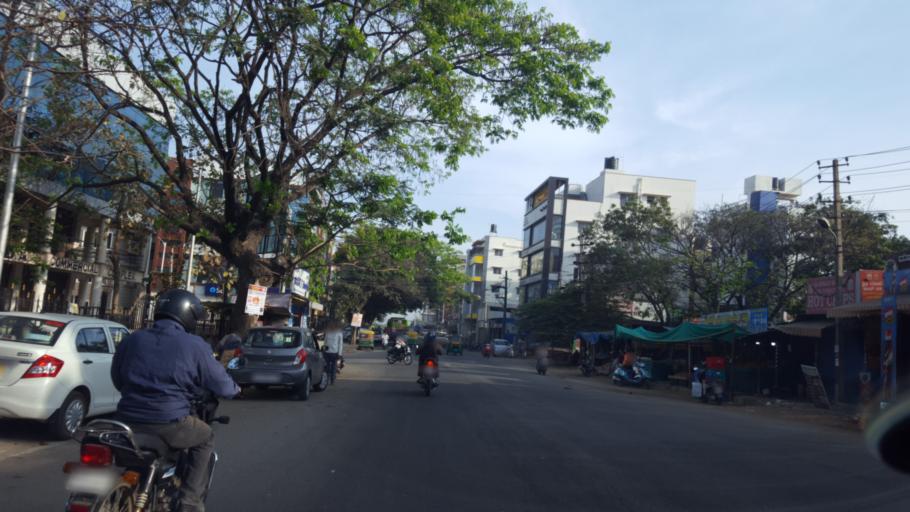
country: IN
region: Karnataka
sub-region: Bangalore Urban
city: Bangalore
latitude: 12.9156
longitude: 77.5134
